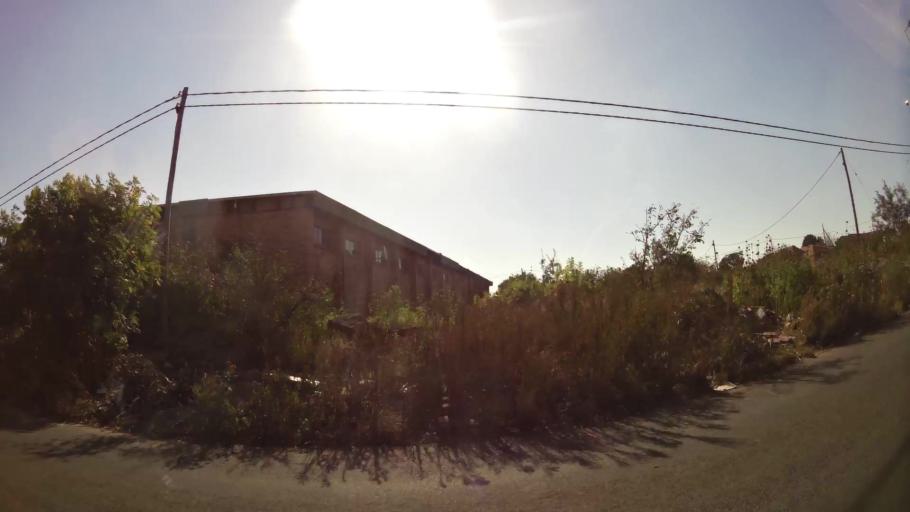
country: ZA
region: Gauteng
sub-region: City of Tshwane Metropolitan Municipality
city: Mabopane
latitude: -25.5340
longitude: 28.0927
